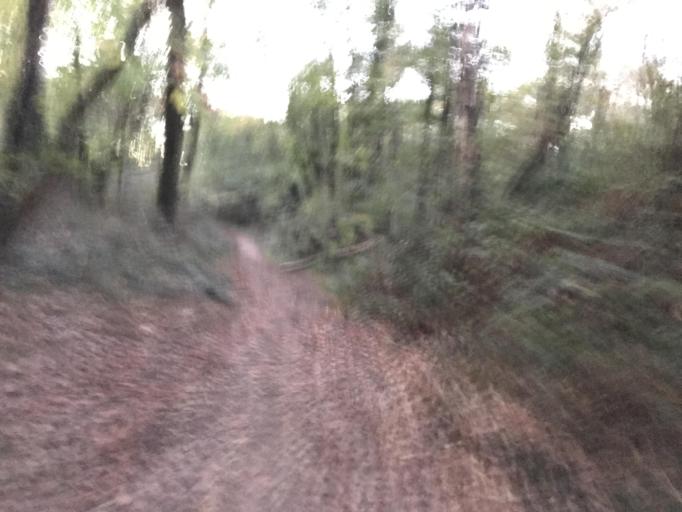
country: FR
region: Ile-de-France
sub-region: Departement de l'Essonne
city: Villejust
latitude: 48.6769
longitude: 2.2458
